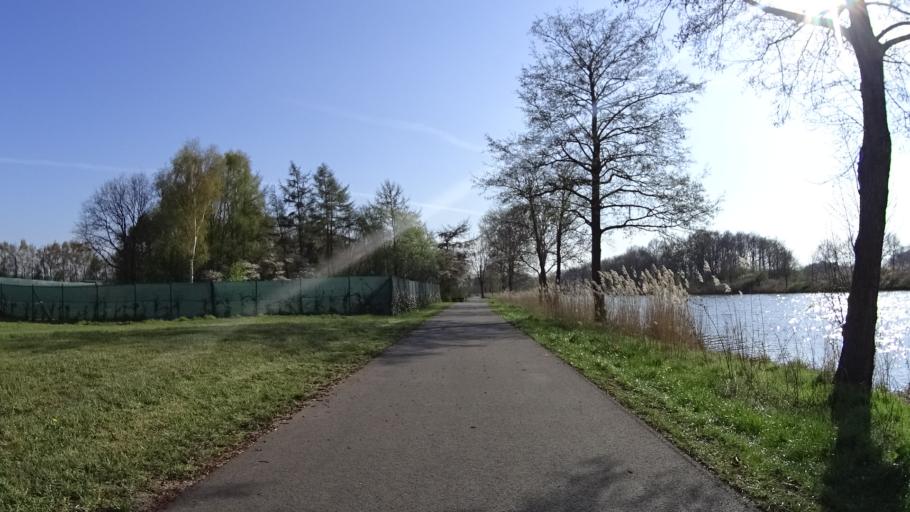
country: DE
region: Lower Saxony
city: Sustrum
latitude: 52.9215
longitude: 7.3022
